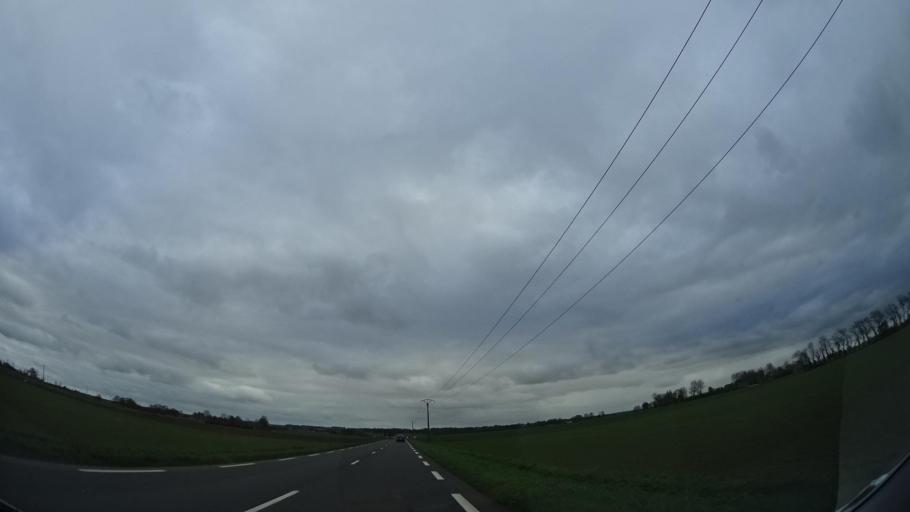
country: FR
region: Haute-Normandie
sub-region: Departement de la Seine-Maritime
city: Cauville-sur-Mer
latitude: 49.5991
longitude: 0.1406
